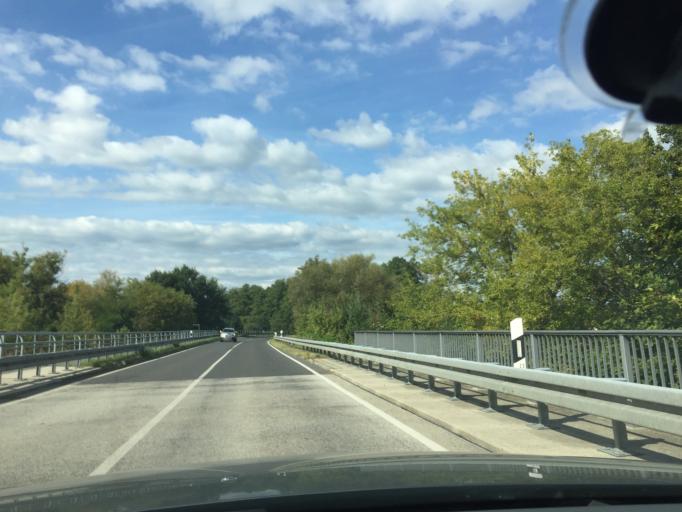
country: DE
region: Brandenburg
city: Spreenhagen
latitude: 52.3603
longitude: 13.8417
